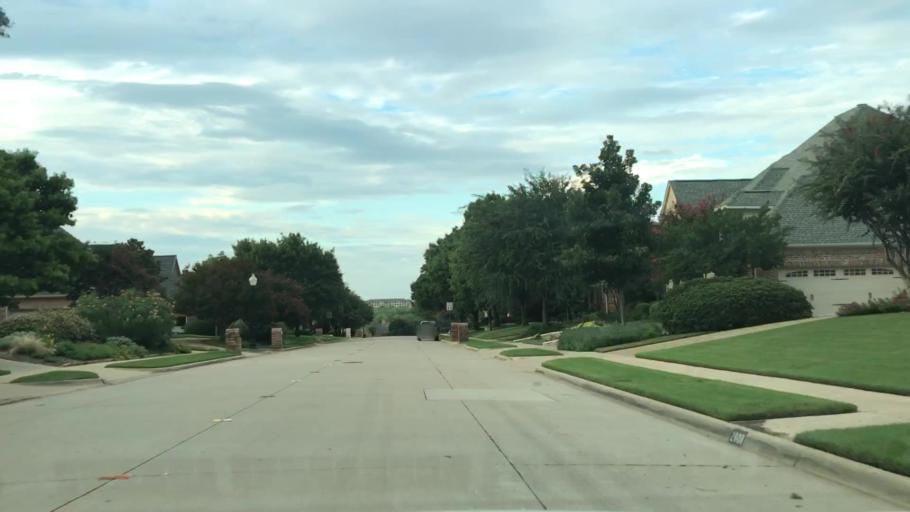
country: US
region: Texas
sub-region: Denton County
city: The Colony
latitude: 33.0402
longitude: -96.8501
